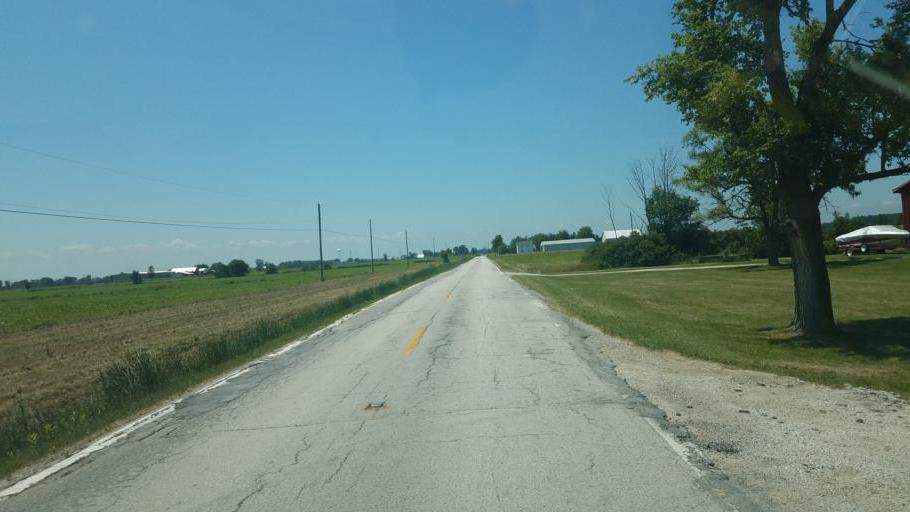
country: US
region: Ohio
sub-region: Ottawa County
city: Oak Harbor
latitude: 41.4428
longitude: -83.1121
